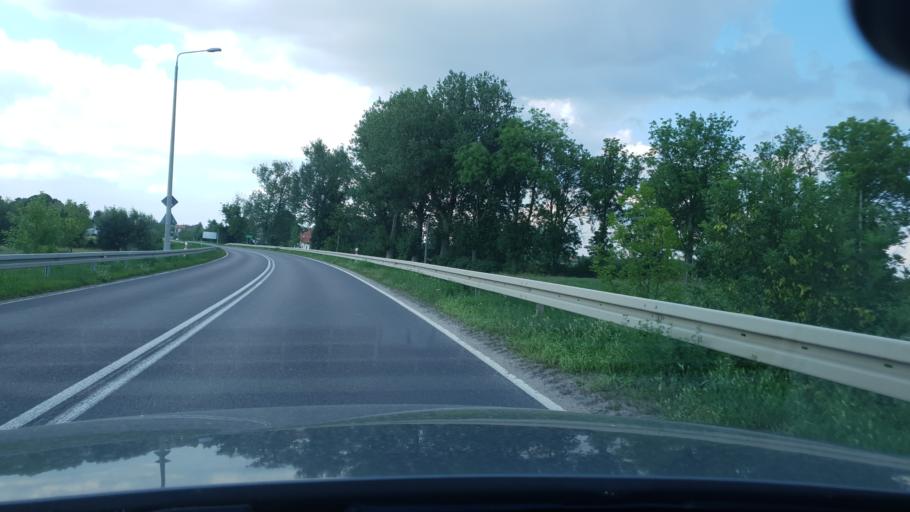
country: PL
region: Kujawsko-Pomorskie
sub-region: Powiat wabrzeski
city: Wabrzezno
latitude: 53.2812
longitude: 18.9296
